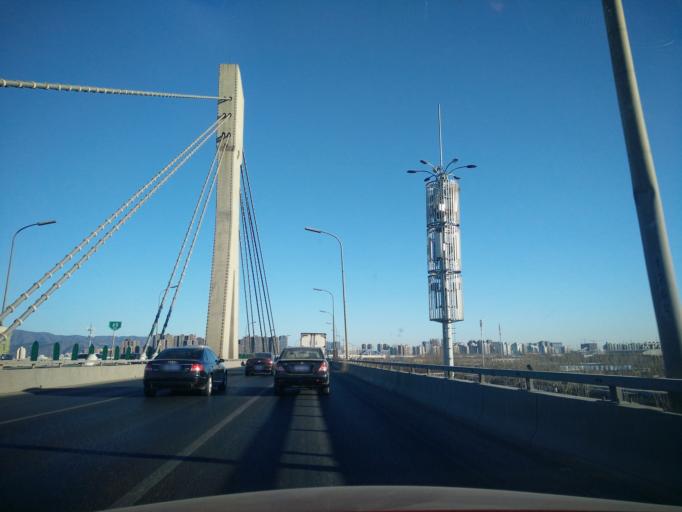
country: CN
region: Beijing
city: Lugu
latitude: 39.8786
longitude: 116.2020
